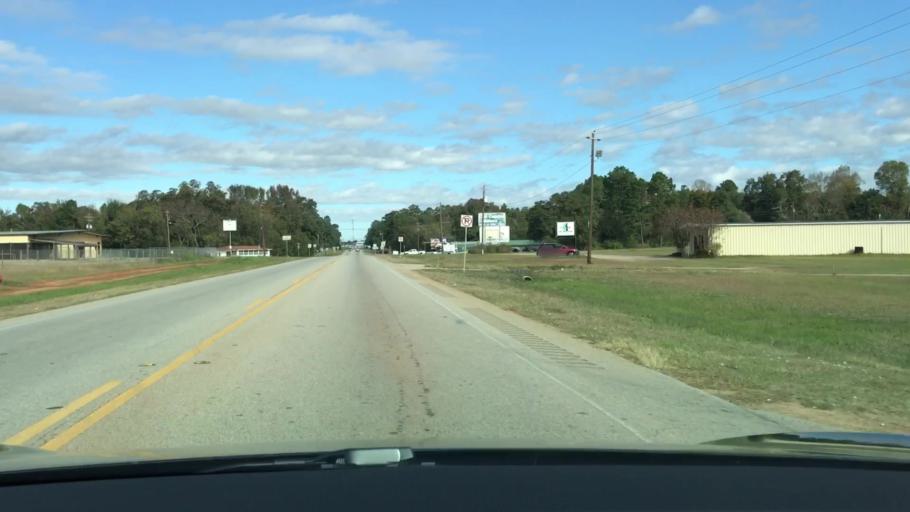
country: US
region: Georgia
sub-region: Jefferson County
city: Louisville
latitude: 32.9934
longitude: -82.3938
